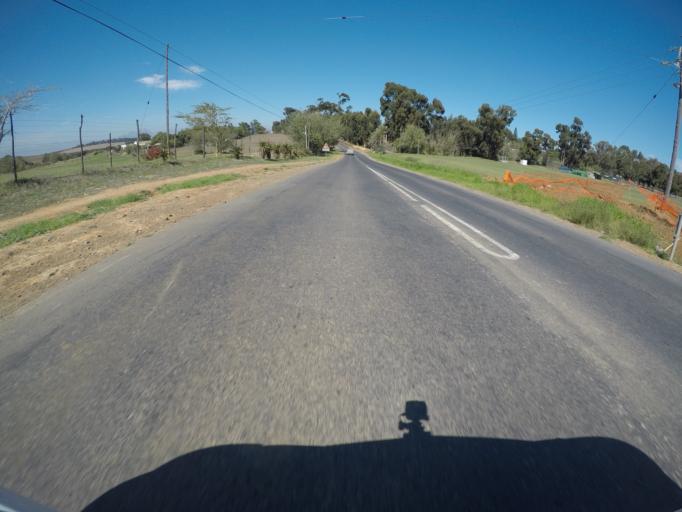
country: ZA
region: Western Cape
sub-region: City of Cape Town
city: Kraaifontein
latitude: -33.8094
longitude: 18.6252
